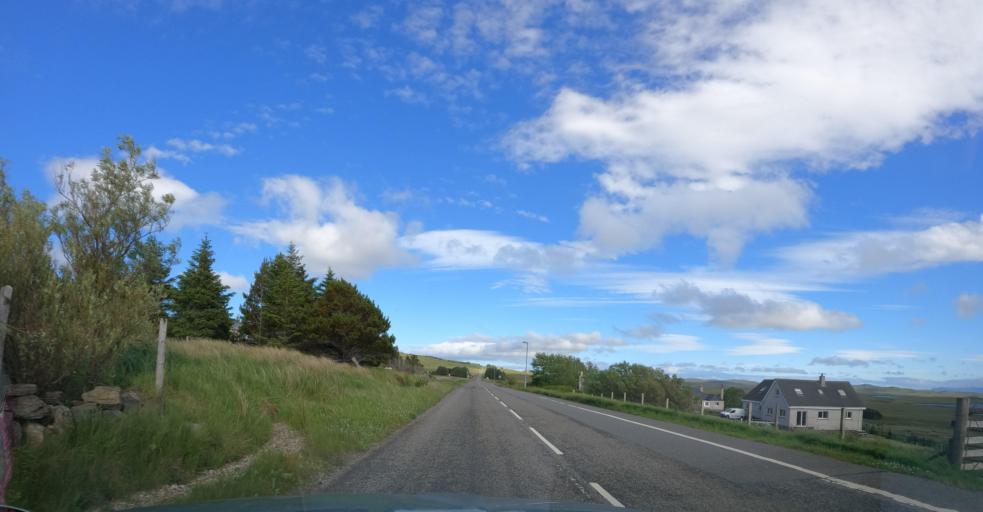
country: GB
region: Scotland
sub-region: Eilean Siar
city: Stornoway
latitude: 58.1744
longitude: -6.6089
